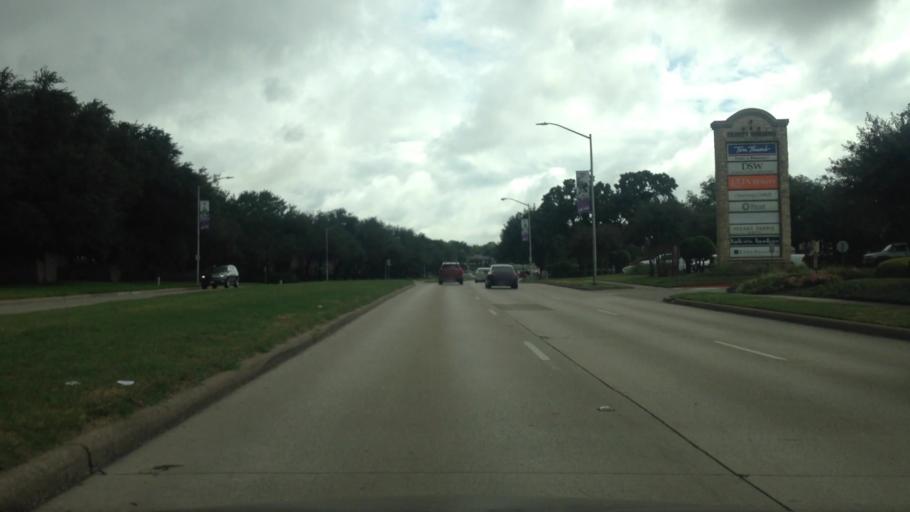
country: US
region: Texas
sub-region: Tarrant County
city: Westworth
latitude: 32.7078
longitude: -97.3875
